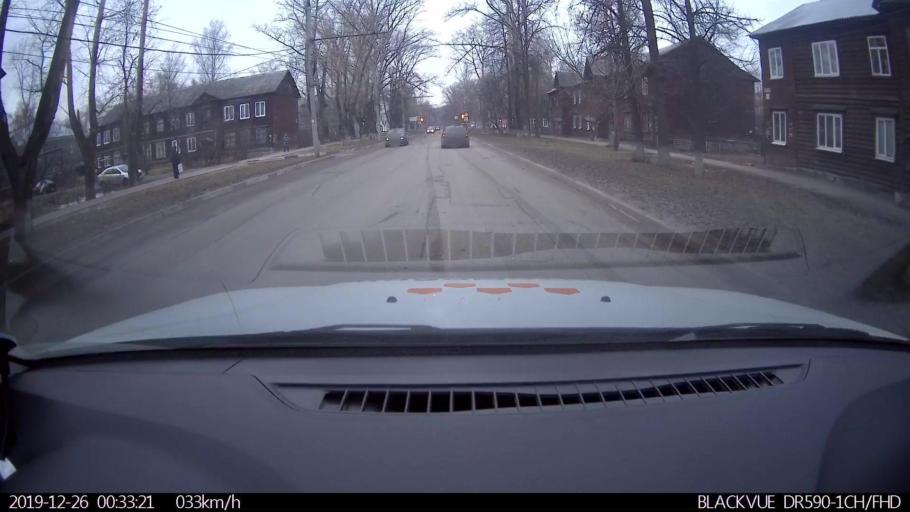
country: RU
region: Nizjnij Novgorod
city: Nizhniy Novgorod
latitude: 56.2884
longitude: 43.9213
